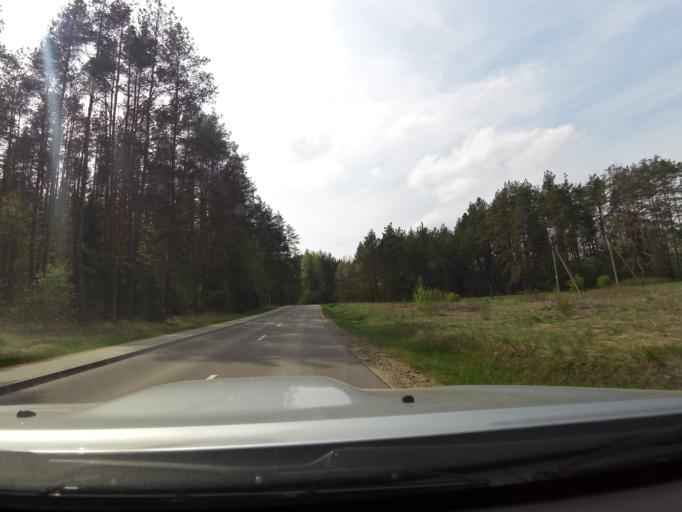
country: LT
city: Salcininkai
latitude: 54.4337
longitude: 25.3234
